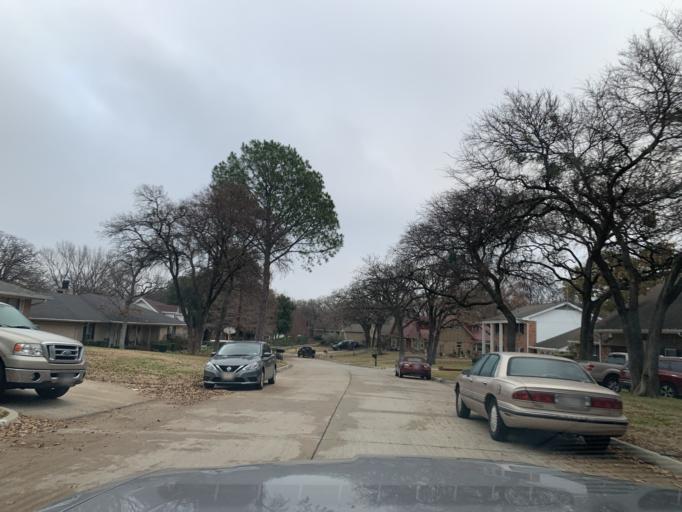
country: US
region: Texas
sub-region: Tarrant County
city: Bedford
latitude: 32.8301
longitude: -97.1534
